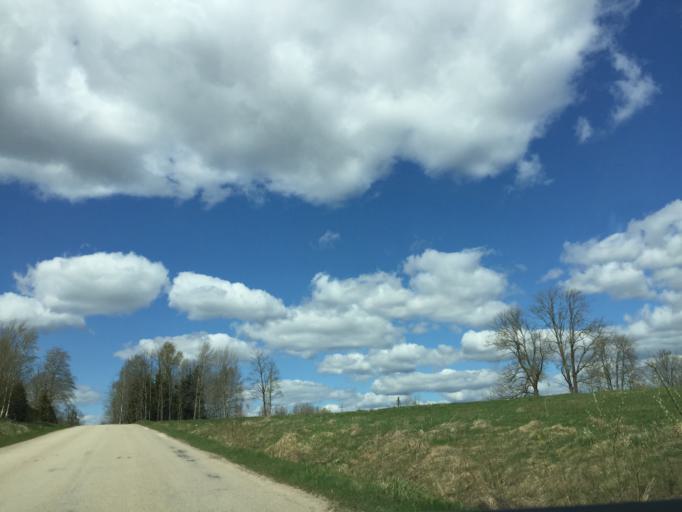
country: LV
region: Rezekne
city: Rezekne
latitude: 56.5577
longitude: 27.1465
